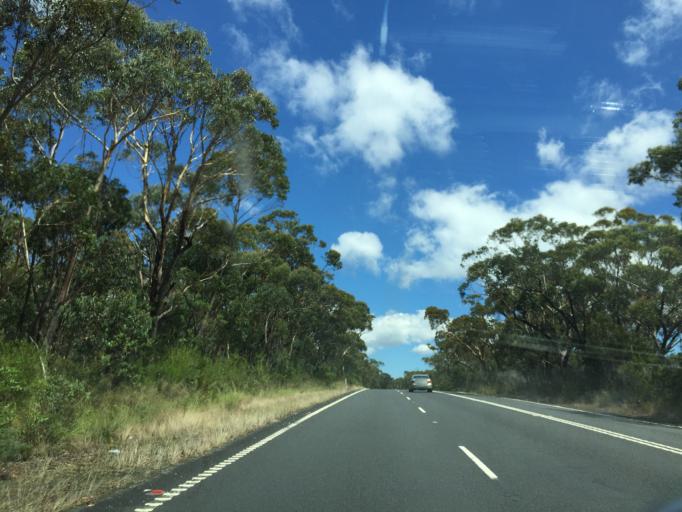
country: AU
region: New South Wales
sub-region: Blue Mountains Municipality
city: Blackheath
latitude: -33.5676
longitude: 150.3629
